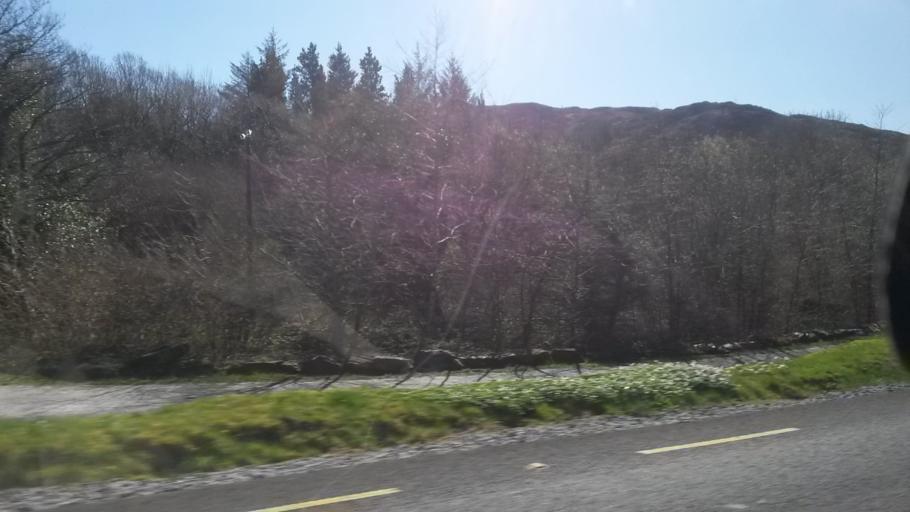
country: IE
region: Munster
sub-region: Ciarrai
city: Cill Airne
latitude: 51.9537
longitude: -9.3895
